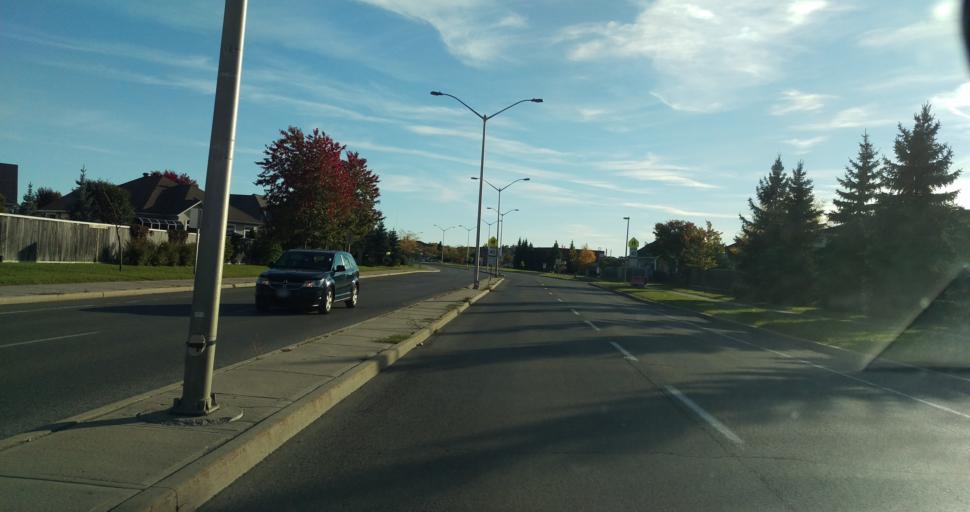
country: CA
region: Ontario
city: Clarence-Rockland
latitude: 45.4656
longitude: -75.4661
